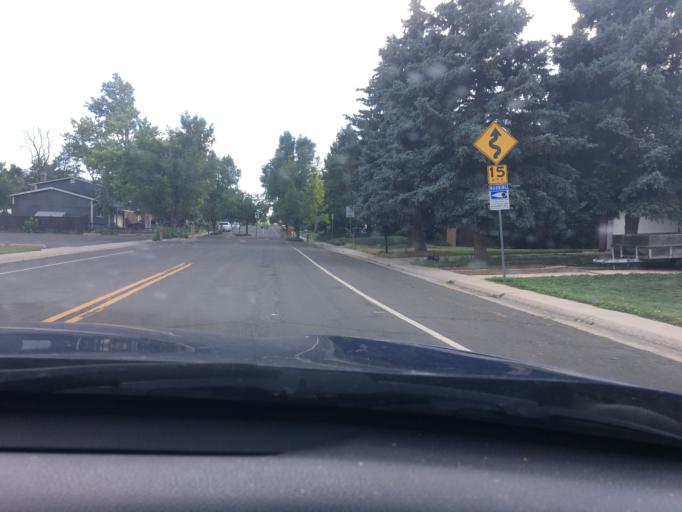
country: US
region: Colorado
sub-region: Jefferson County
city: Applewood
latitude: 39.7675
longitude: -105.1380
